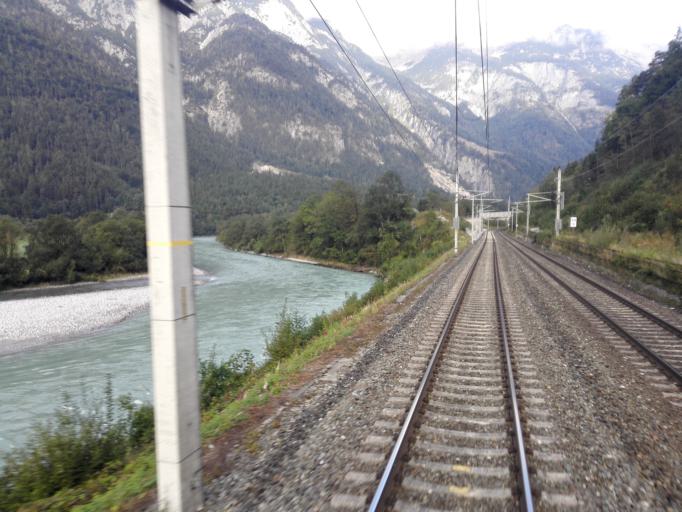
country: AT
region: Salzburg
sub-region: Politischer Bezirk Sankt Johann im Pongau
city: Werfen
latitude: 47.5053
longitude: 13.1742
